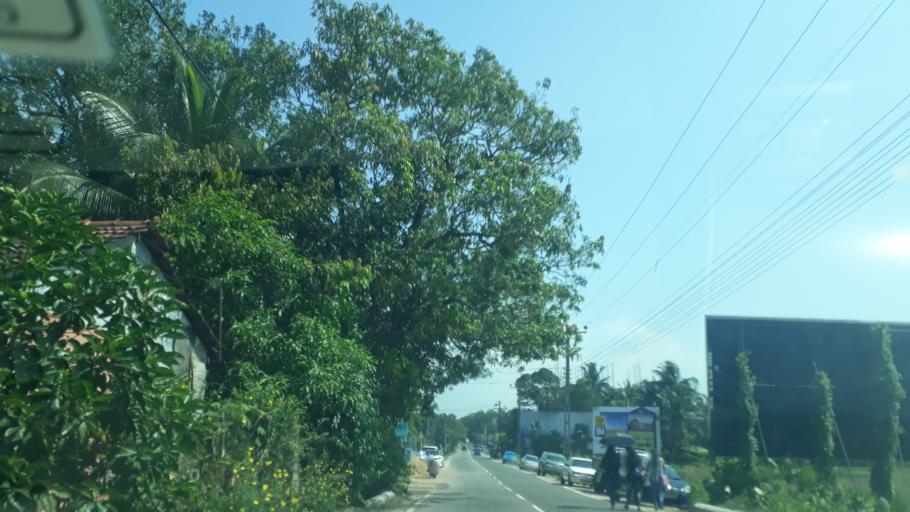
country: LK
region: Western
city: Gampaha
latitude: 7.0783
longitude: 80.0128
